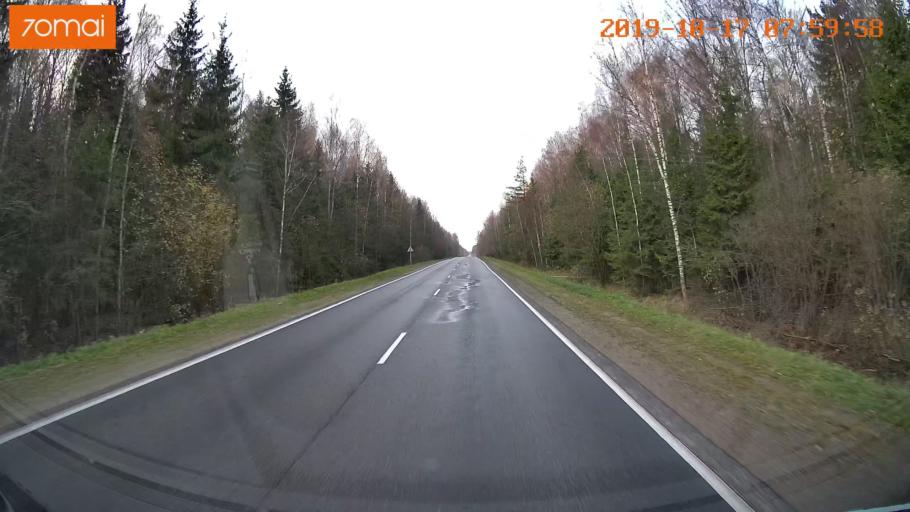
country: RU
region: Vladimir
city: Bavleny
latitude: 56.3882
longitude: 39.5278
